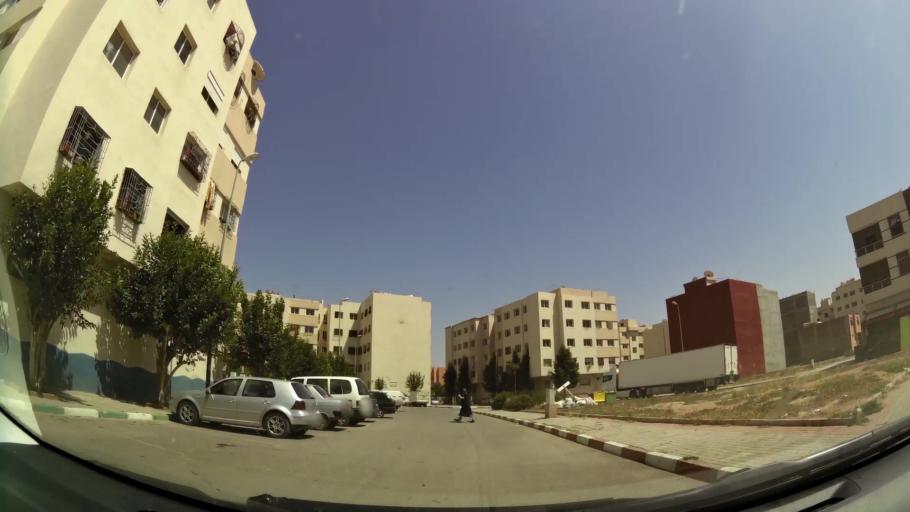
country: MA
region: Souss-Massa-Draa
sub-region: Inezgane-Ait Mellou
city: Inezgane
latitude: 30.3430
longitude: -9.5152
